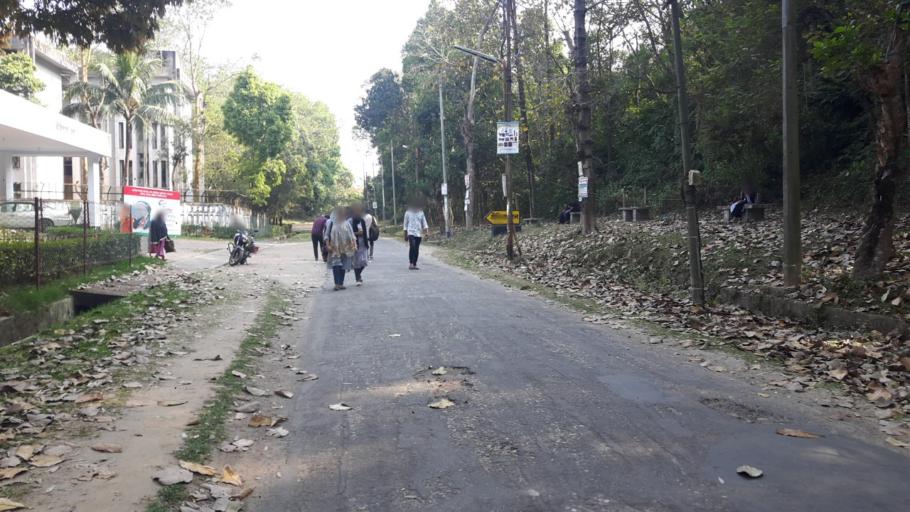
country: BD
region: Chittagong
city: Chittagong
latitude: 22.4680
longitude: 91.7884
